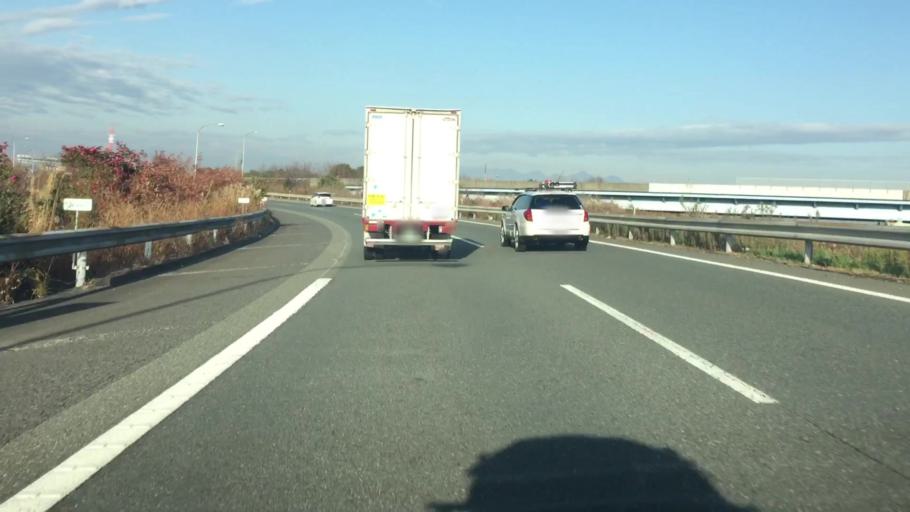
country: JP
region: Gunma
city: Fujioka
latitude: 36.2721
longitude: 139.0948
